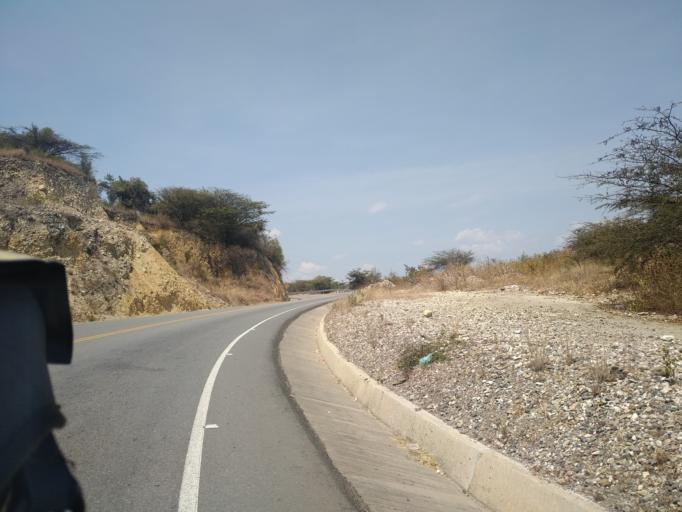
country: PE
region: Cajamarca
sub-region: Provincia de Cajabamba
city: Cauday
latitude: -7.6116
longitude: -78.0857
